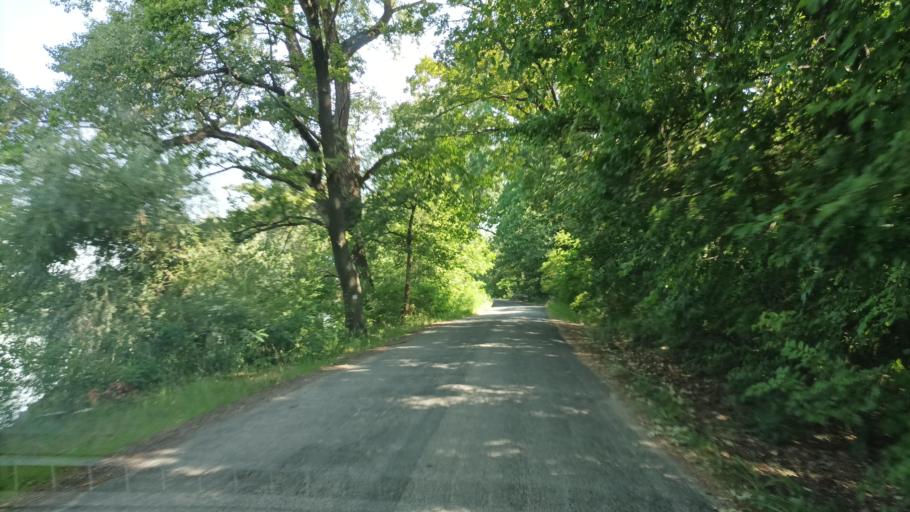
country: HU
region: Pest
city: Szigetujfalu
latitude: 47.2365
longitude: 18.9141
